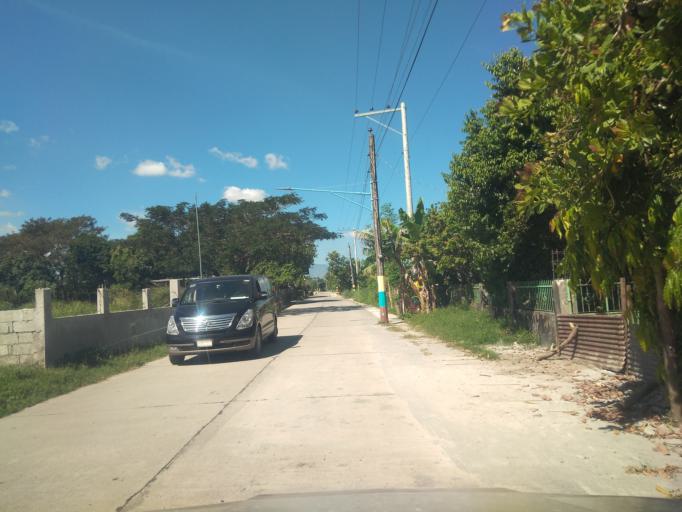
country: PH
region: Central Luzon
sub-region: Province of Pampanga
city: Magliman
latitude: 15.0279
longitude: 120.6350
